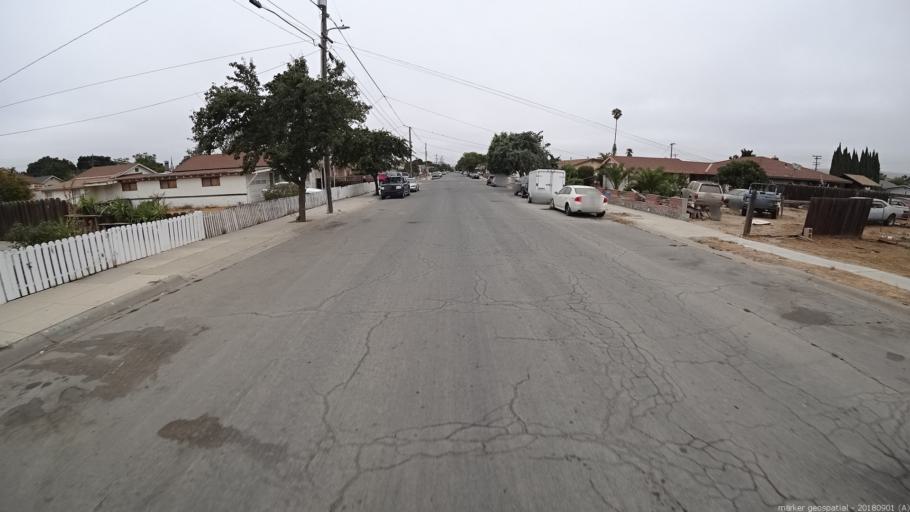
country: US
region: California
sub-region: Monterey County
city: Greenfield
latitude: 36.3176
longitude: -121.2437
